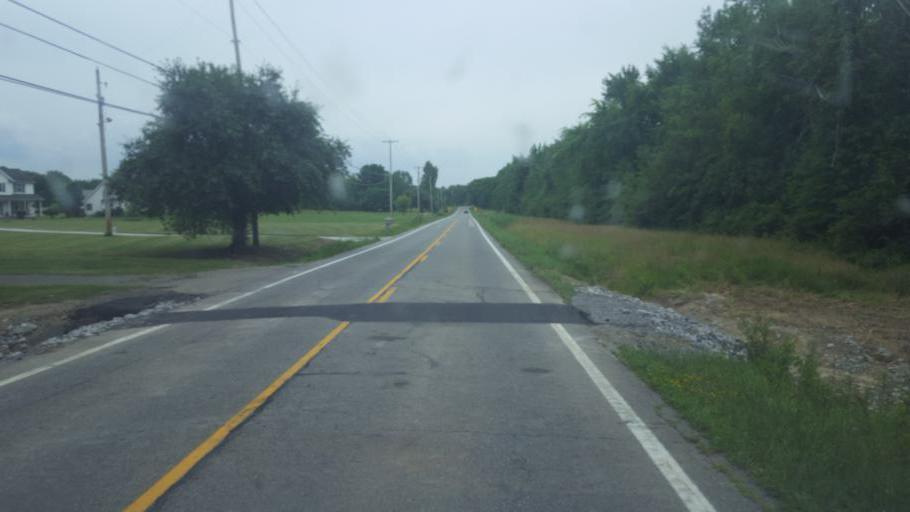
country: US
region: Ohio
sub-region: Trumbull County
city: Cortland
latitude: 41.3513
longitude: -80.7352
